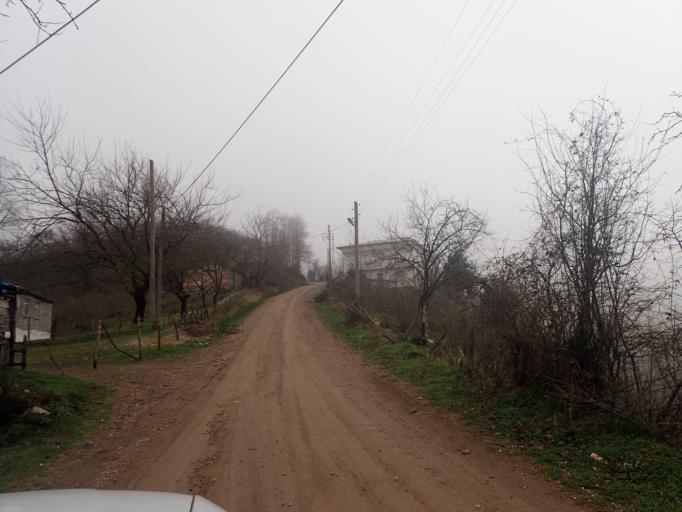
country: TR
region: Ordu
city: Camas
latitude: 40.9091
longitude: 37.5669
